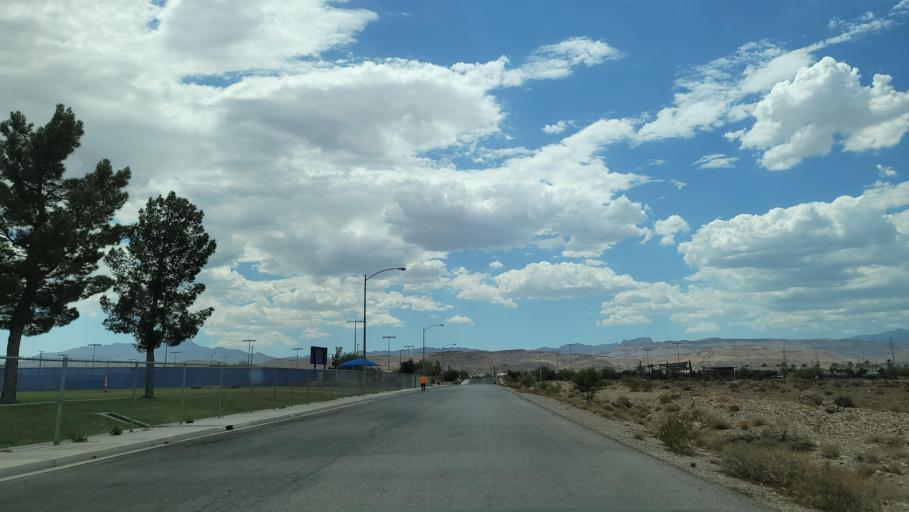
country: US
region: Nevada
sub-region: Clark County
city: Enterprise
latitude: 36.0519
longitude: -115.2679
